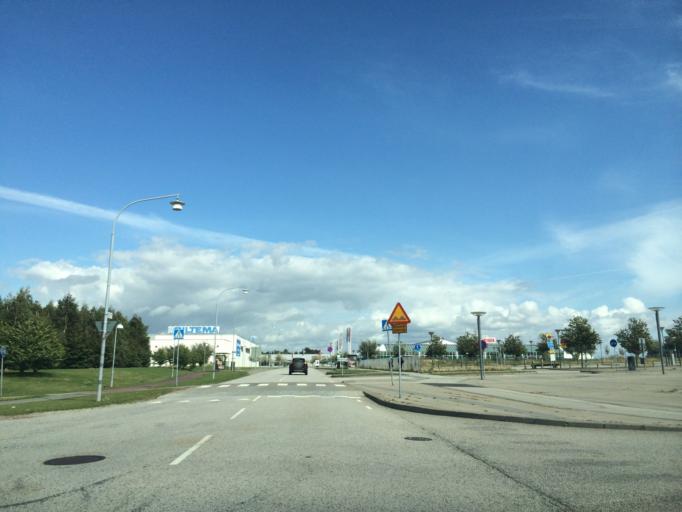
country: SE
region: Skane
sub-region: Malmo
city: Tygelsjo
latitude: 55.5490
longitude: 12.9903
